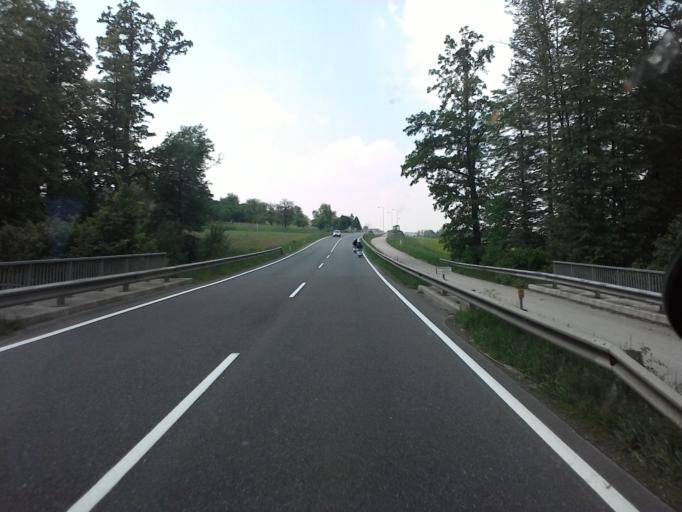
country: AT
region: Upper Austria
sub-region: Politischer Bezirk Steyr-Land
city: Bad Hall
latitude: 48.0264
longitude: 14.2381
